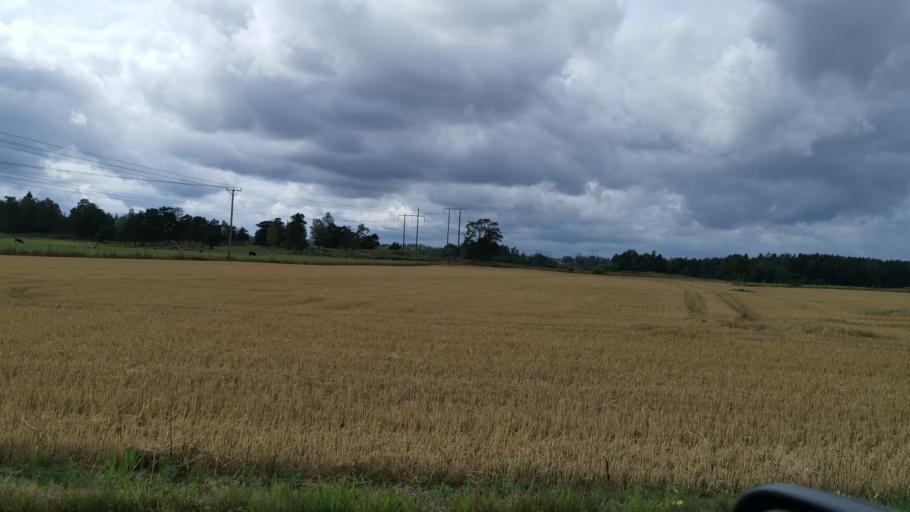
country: SE
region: Vaestra Goetaland
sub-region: Vanersborgs Kommun
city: Vanersborg
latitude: 58.3453
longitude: 12.3189
